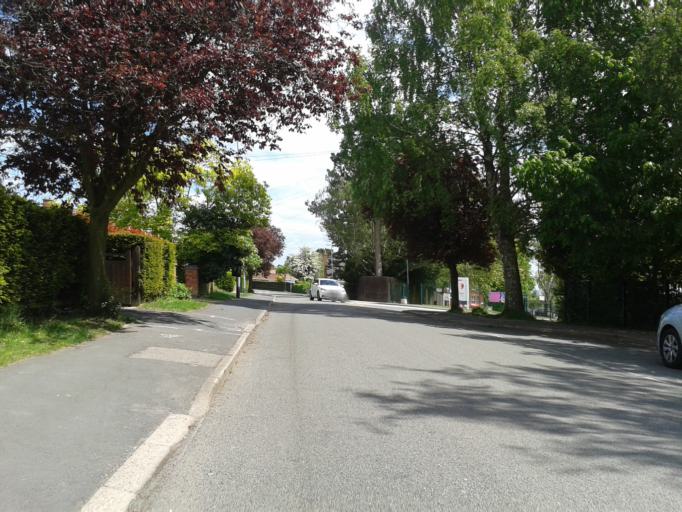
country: GB
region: England
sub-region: Leicestershire
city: Hinckley
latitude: 52.5469
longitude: -1.3559
